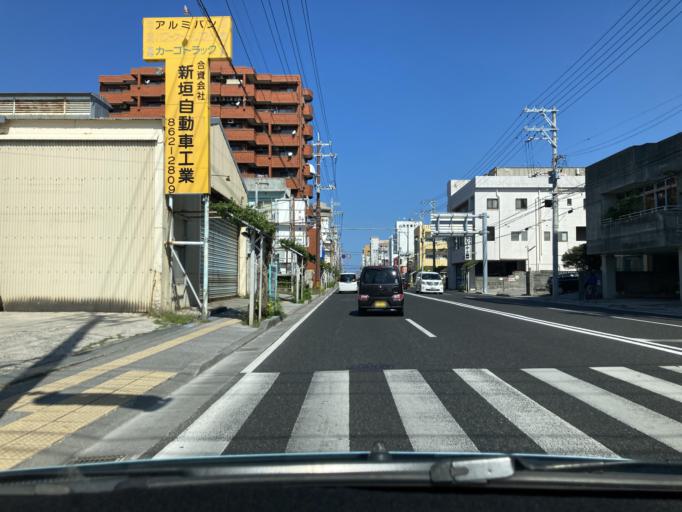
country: JP
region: Okinawa
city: Naha-shi
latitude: 26.2369
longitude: 127.6816
